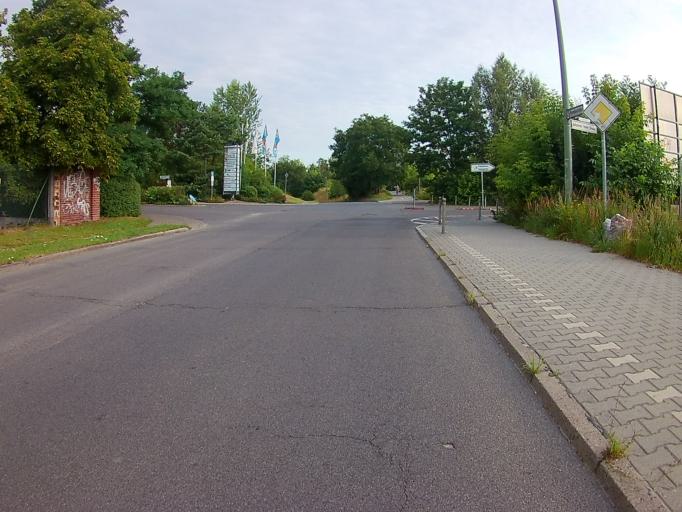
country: DE
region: Berlin
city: Bohnsdorf
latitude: 52.4049
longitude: 13.5602
